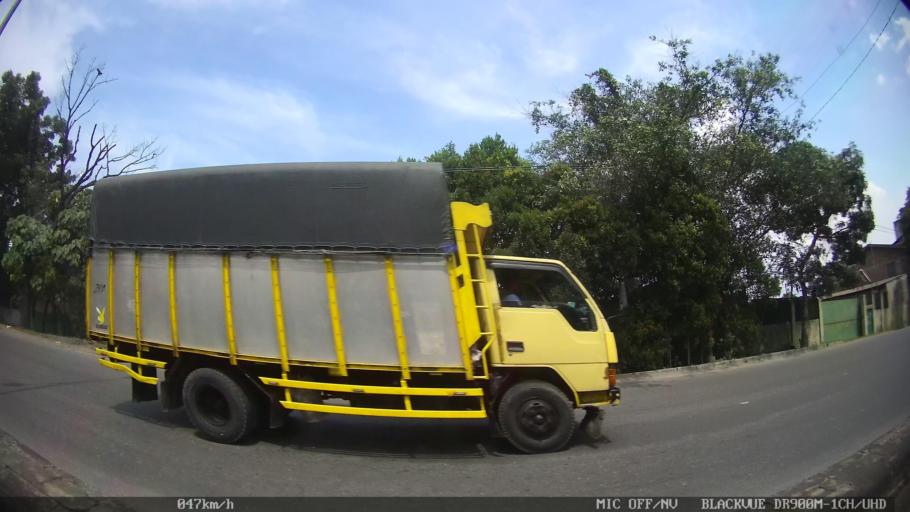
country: ID
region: North Sumatra
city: Labuhan Deli
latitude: 3.6672
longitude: 98.6670
